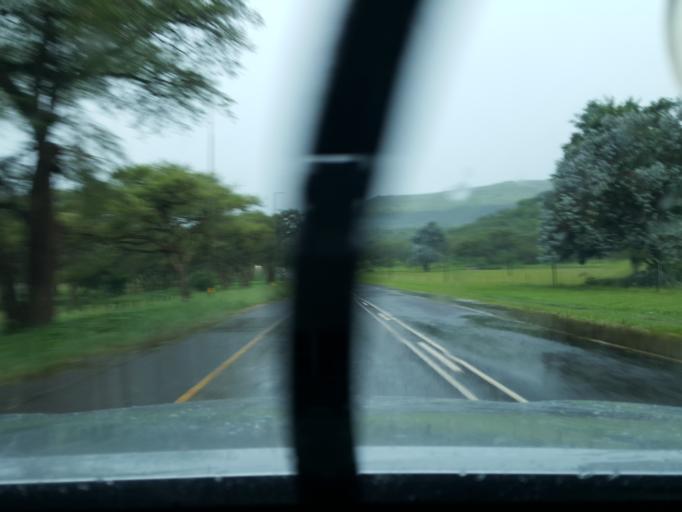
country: ZA
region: Mpumalanga
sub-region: Ehlanzeni District
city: Nelspruit
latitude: -25.5851
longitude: 30.6437
